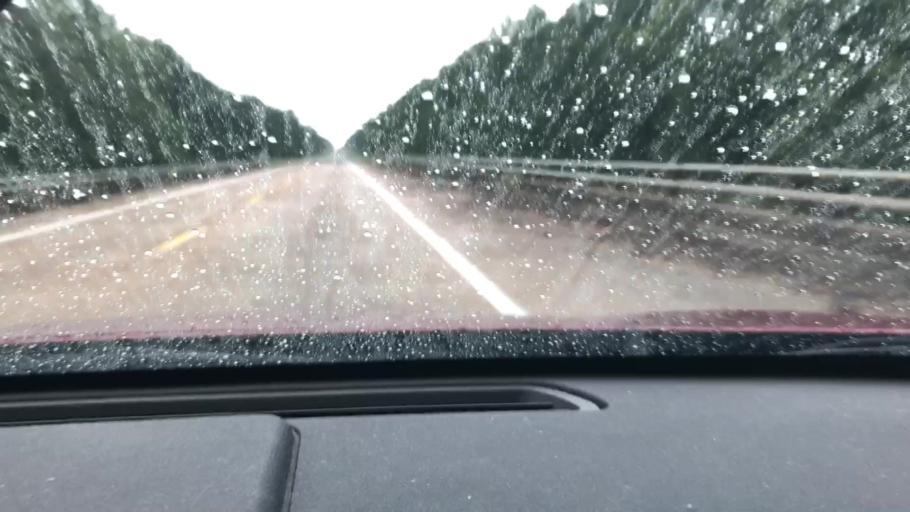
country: US
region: Arkansas
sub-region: Columbia County
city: Magnolia
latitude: 33.3031
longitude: -93.2700
